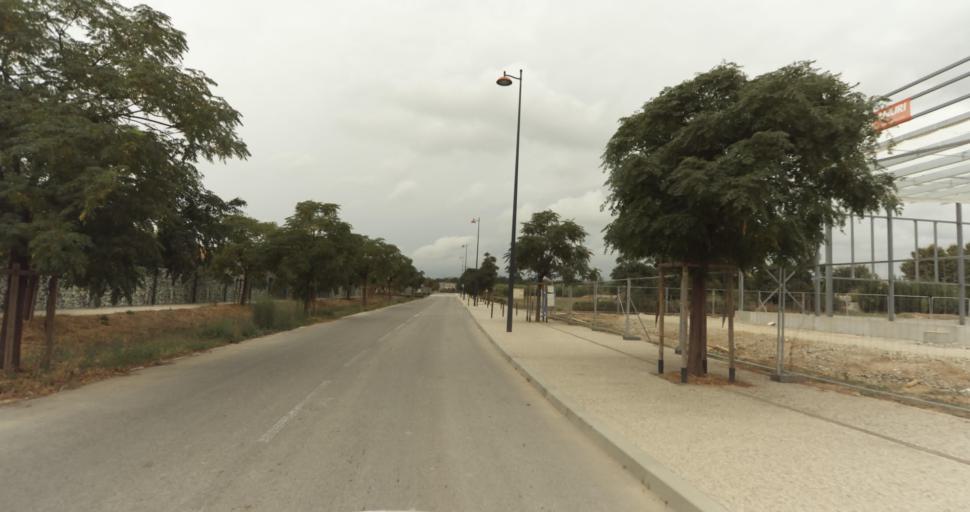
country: FR
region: Provence-Alpes-Cote d'Azur
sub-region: Departement des Bouches-du-Rhone
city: Saint-Victoret
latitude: 43.4151
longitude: 5.2598
